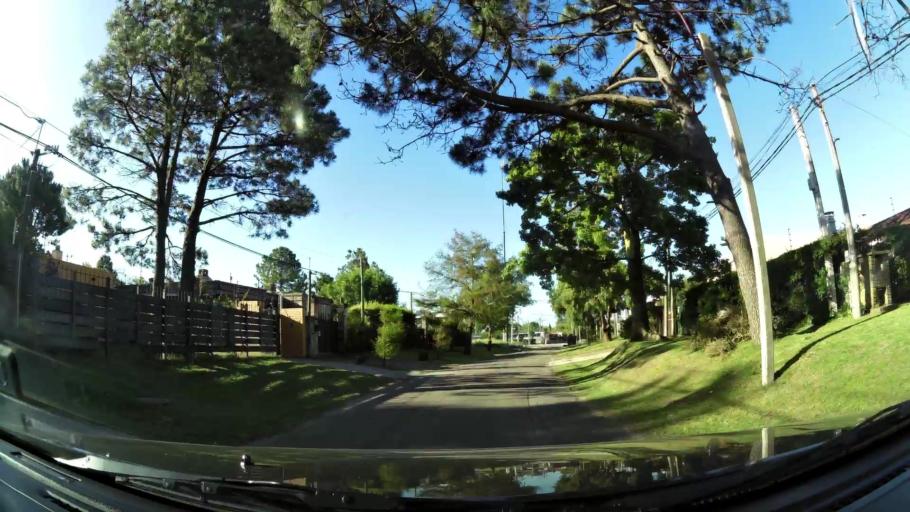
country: UY
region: Canelones
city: Paso de Carrasco
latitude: -34.8713
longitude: -56.0548
